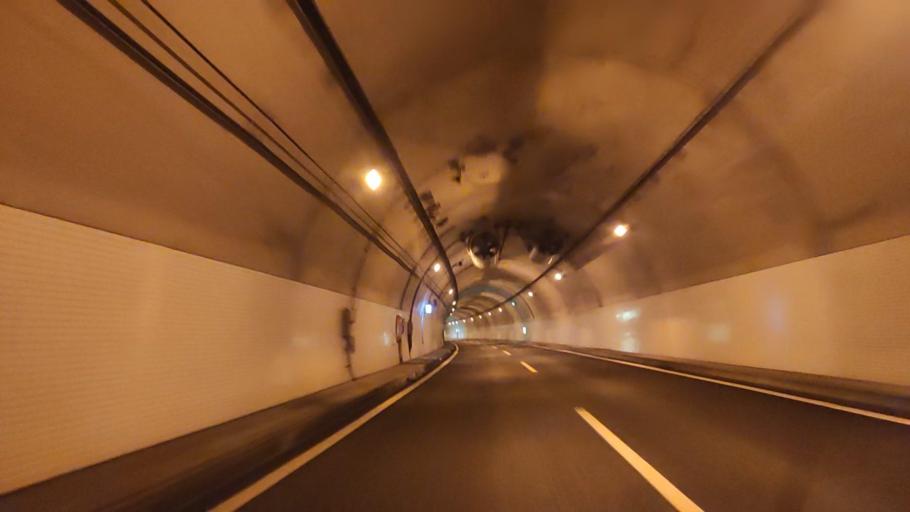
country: JP
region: Niigata
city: Itoigawa
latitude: 37.0069
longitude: 137.7454
